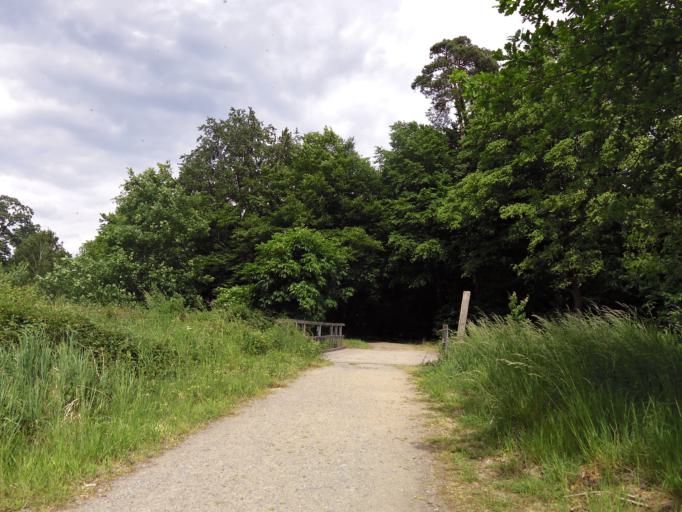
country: DE
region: Hesse
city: Morfelden-Walldorf
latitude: 50.0185
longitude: 8.5806
